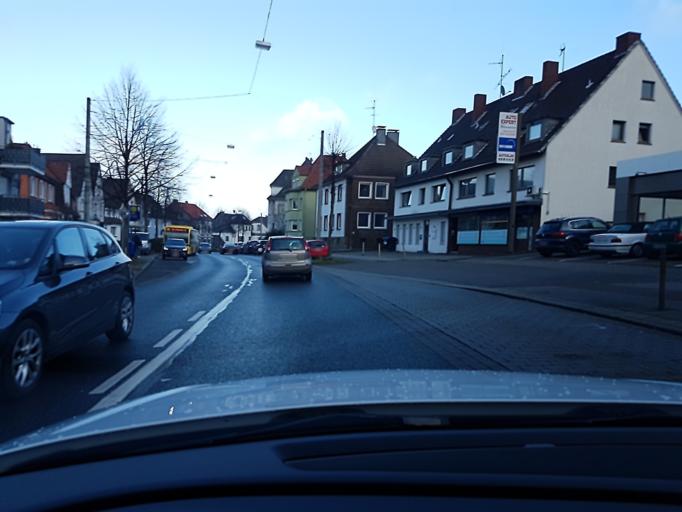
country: DE
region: North Rhine-Westphalia
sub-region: Regierungsbezirk Dusseldorf
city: Essen
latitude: 51.4223
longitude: 7.0284
